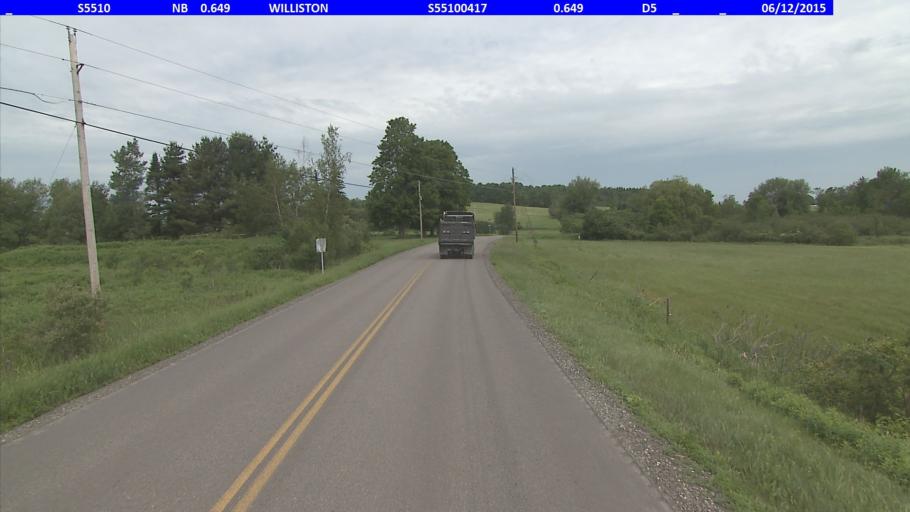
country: US
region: Vermont
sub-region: Chittenden County
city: Hinesburg
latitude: 44.3818
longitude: -73.0973
